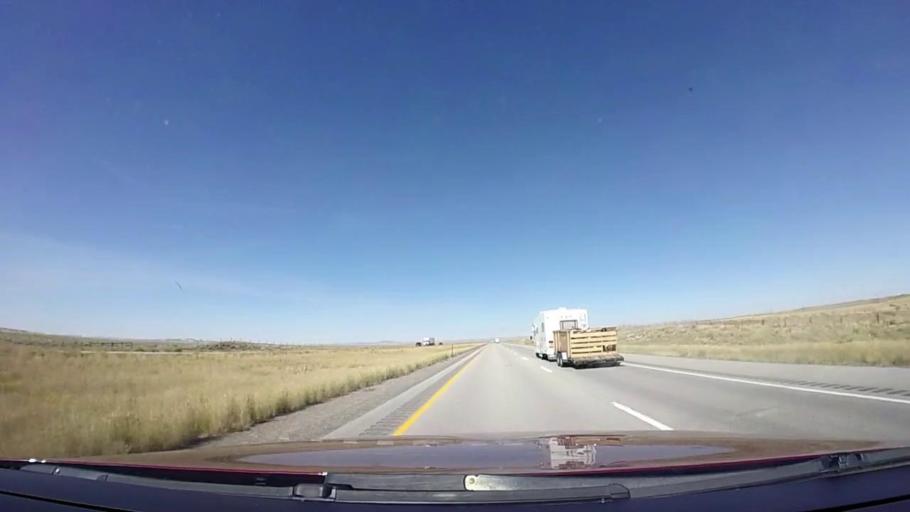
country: US
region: Wyoming
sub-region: Sweetwater County
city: Rock Springs
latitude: 41.6313
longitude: -108.3393
